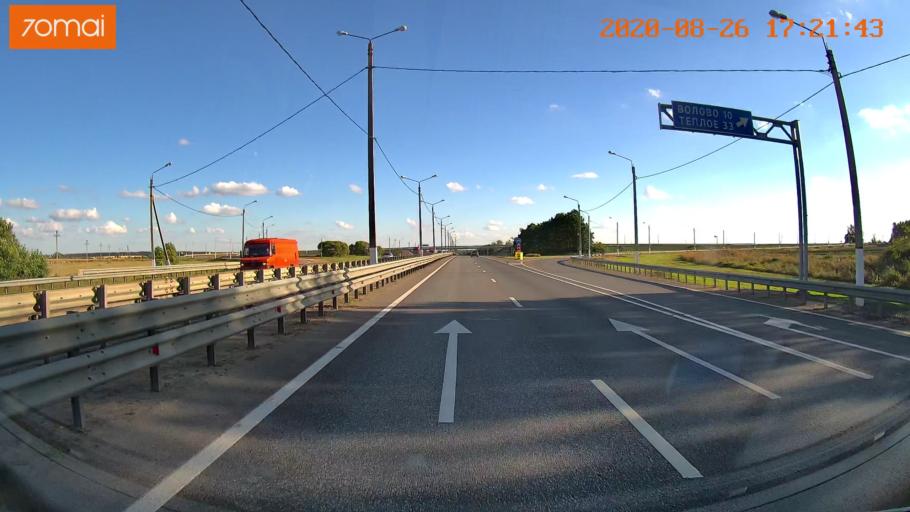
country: RU
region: Tula
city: Volovo
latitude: 53.5607
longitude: 38.1122
